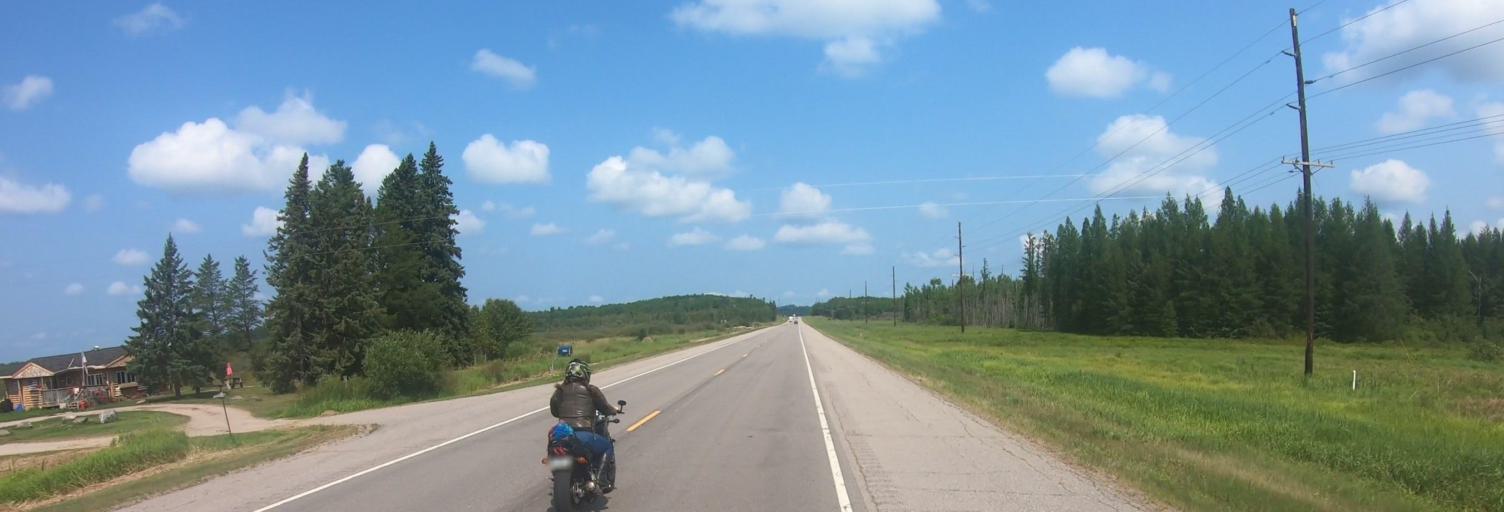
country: US
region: Minnesota
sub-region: Saint Louis County
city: Chisholm
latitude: 47.9450
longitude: -92.8288
